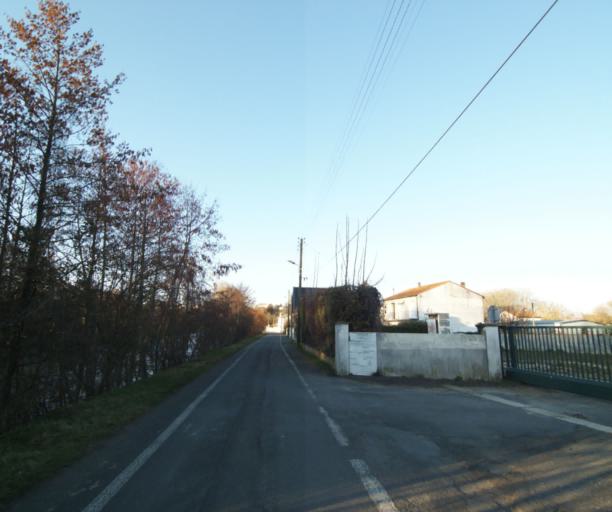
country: FR
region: Poitou-Charentes
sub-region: Departement des Deux-Sevres
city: Niort
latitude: 46.3316
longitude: -0.4787
